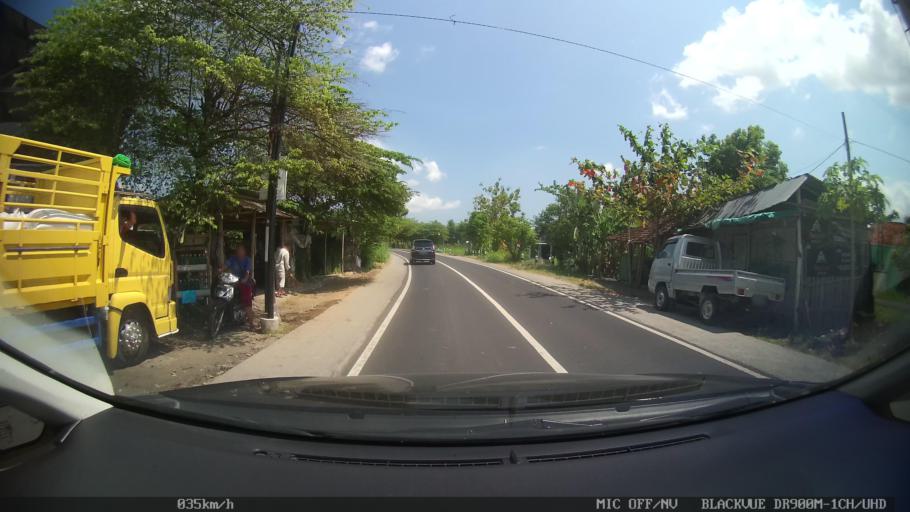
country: ID
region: Daerah Istimewa Yogyakarta
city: Pundong
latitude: -7.9189
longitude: 110.3773
